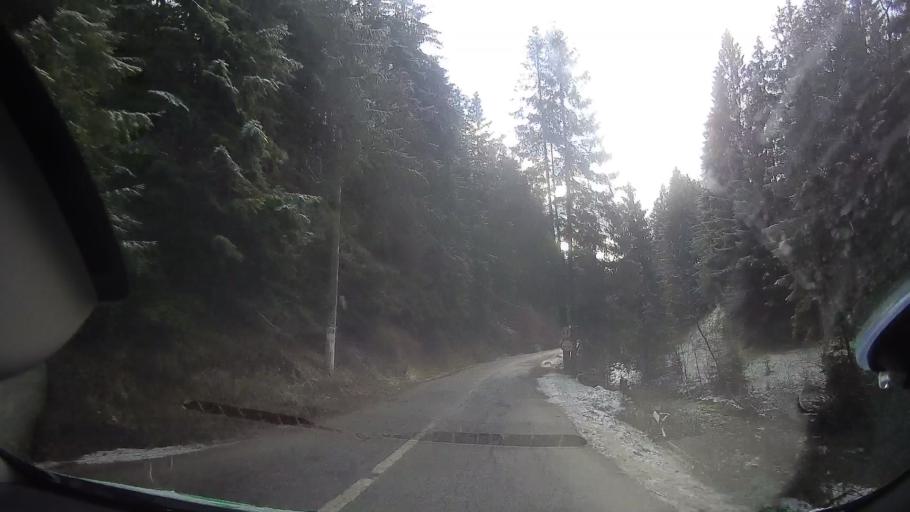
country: RO
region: Alba
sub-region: Comuna Horea
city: Horea
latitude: 46.4930
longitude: 22.9617
